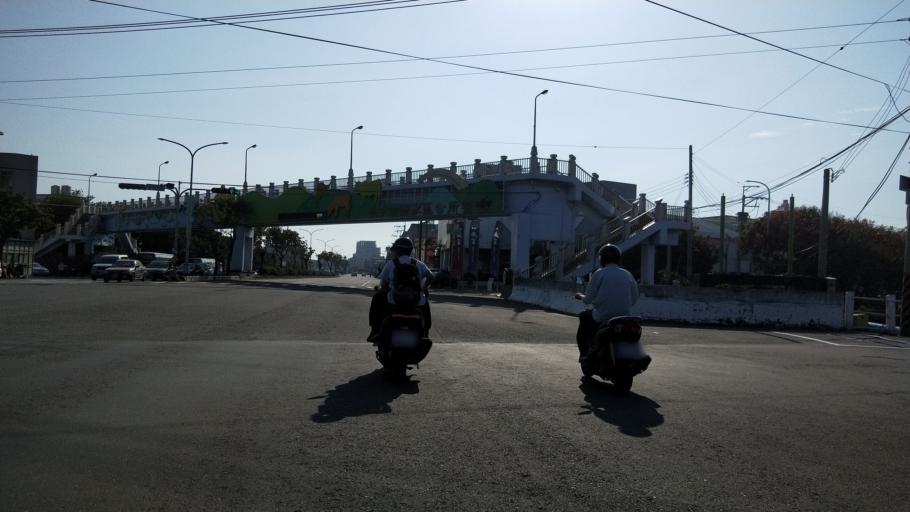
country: TW
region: Taiwan
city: Fengyuan
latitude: 24.2784
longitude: 120.5755
